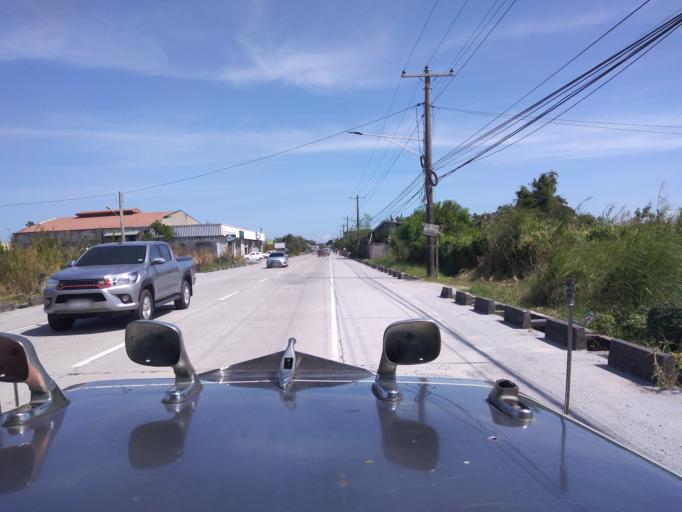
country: PH
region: Central Luzon
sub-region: Province of Pampanga
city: San Juan
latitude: 15.0163
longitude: 120.6676
